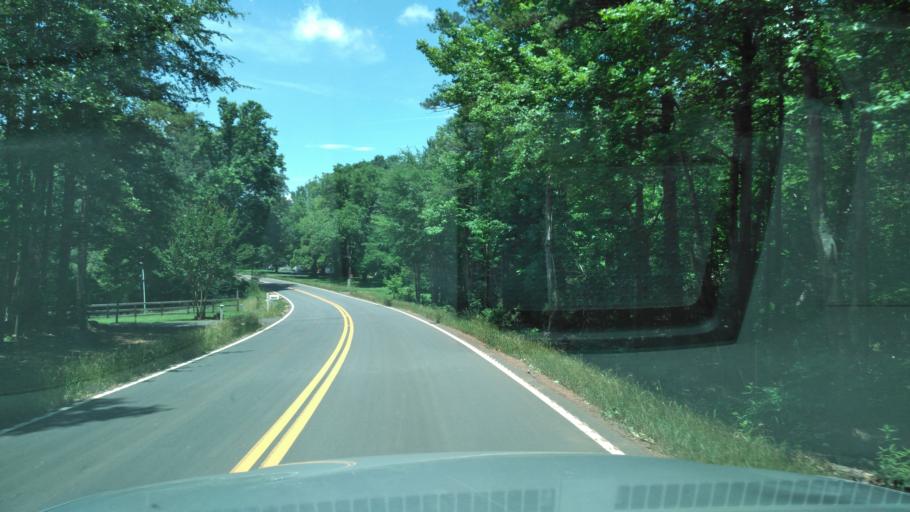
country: US
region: South Carolina
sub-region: Greenwood County
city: Ware Shoals
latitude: 34.4223
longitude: -82.1313
